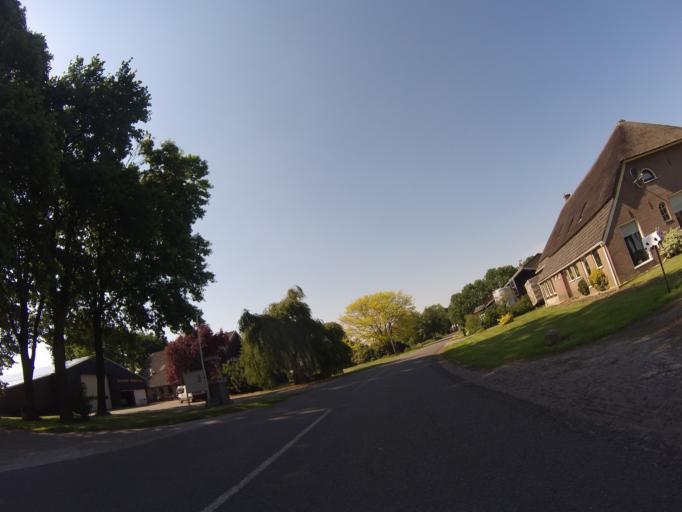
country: NL
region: Drenthe
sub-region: Gemeente Coevorden
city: Dalen
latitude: 52.7162
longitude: 6.8013
